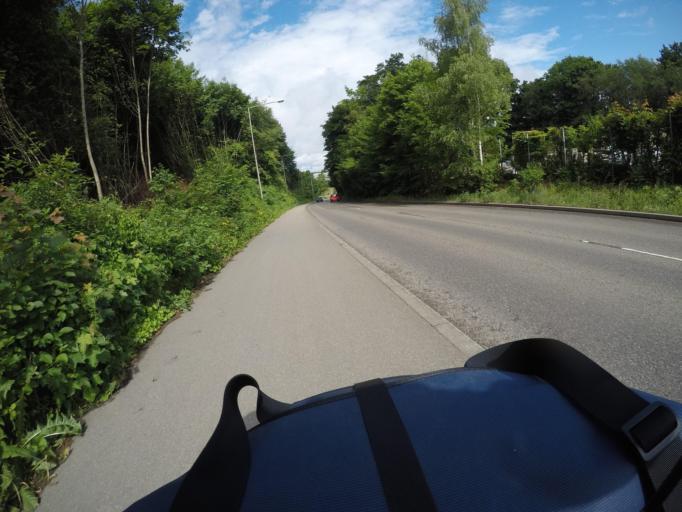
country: DE
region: Baden-Wuerttemberg
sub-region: Regierungsbezirk Stuttgart
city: Gerlingen
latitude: 48.7407
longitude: 9.0893
